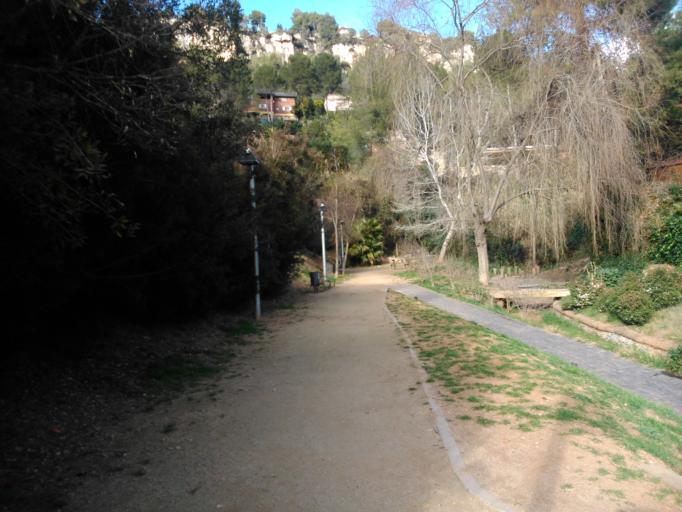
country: ES
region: Catalonia
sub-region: Provincia de Barcelona
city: Cervello
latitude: 41.4148
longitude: 1.9698
